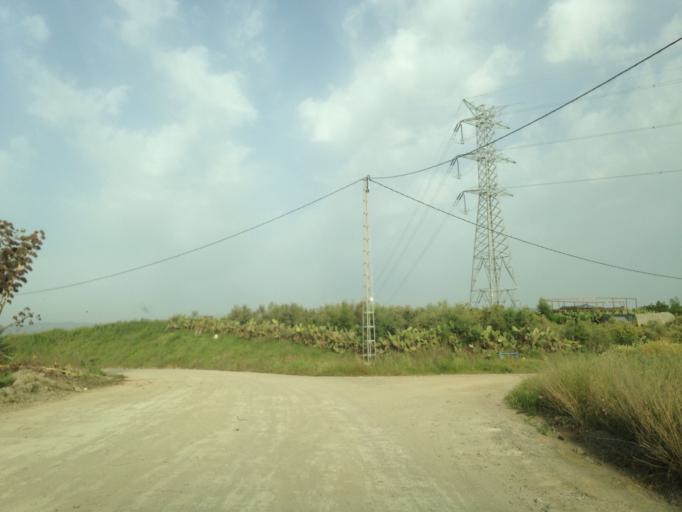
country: ES
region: Andalusia
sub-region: Provincia de Malaga
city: Estacion de Cartama
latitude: 36.7542
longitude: -4.5551
